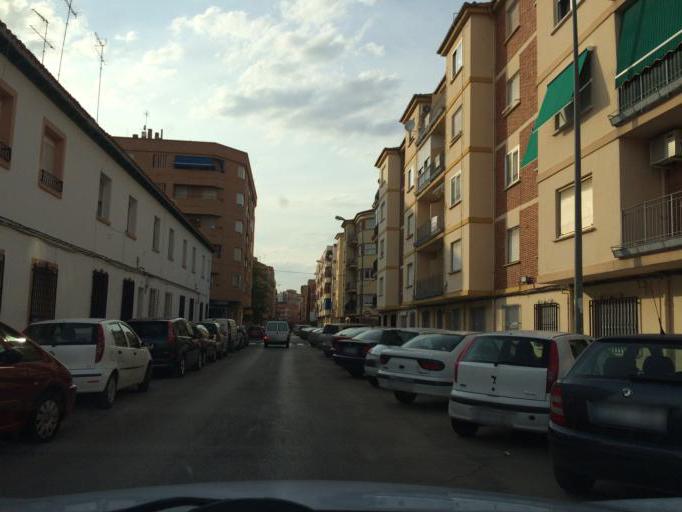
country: ES
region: Castille-La Mancha
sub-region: Provincia de Albacete
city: Albacete
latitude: 38.9866
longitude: -1.8626
